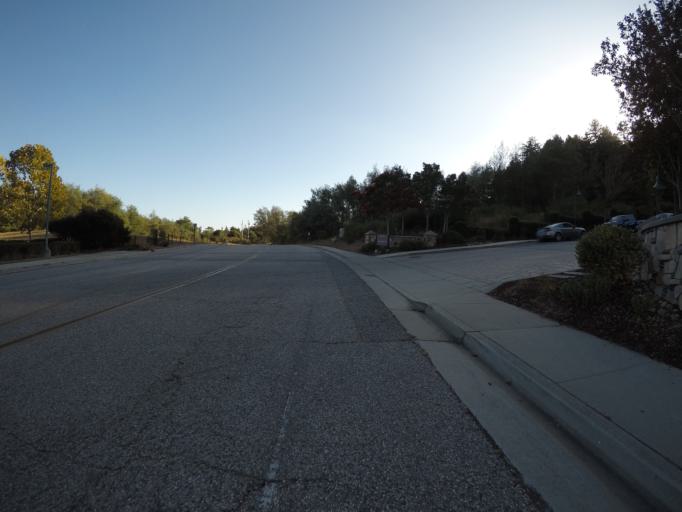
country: US
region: California
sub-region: Santa Cruz County
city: Scotts Valley
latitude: 37.0359
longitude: -122.0232
